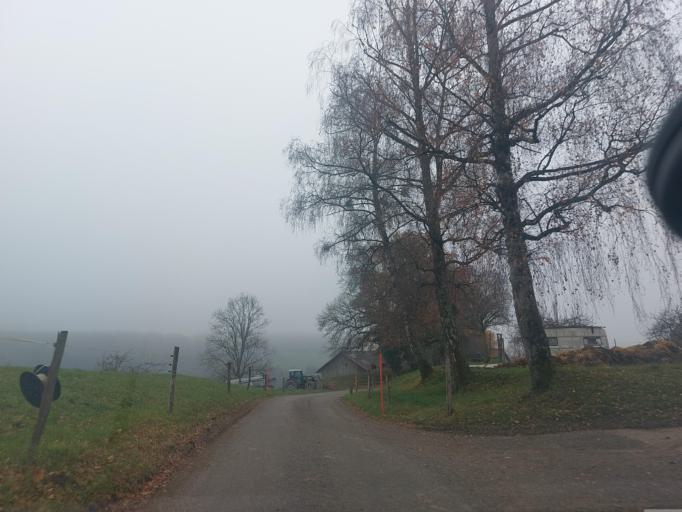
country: CH
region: Vaud
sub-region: Lavaux-Oron District
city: Oron-la-ville
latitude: 46.5720
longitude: 6.8640
